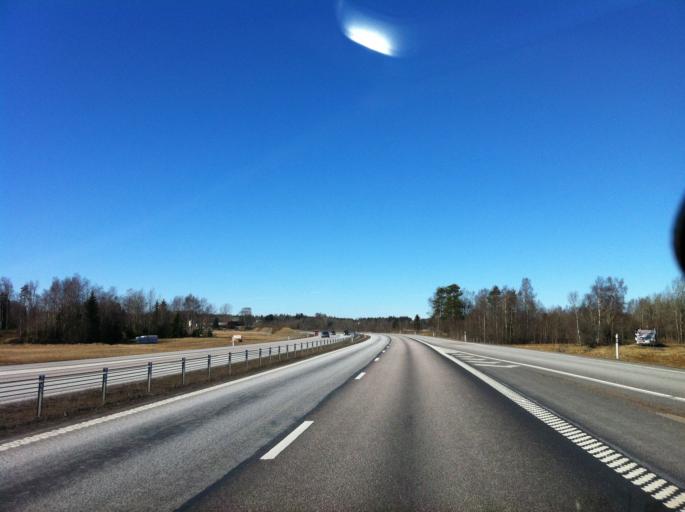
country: SE
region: Vaestra Goetaland
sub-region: Vanersborgs Kommun
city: Vanersborg
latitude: 58.3721
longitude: 12.3460
